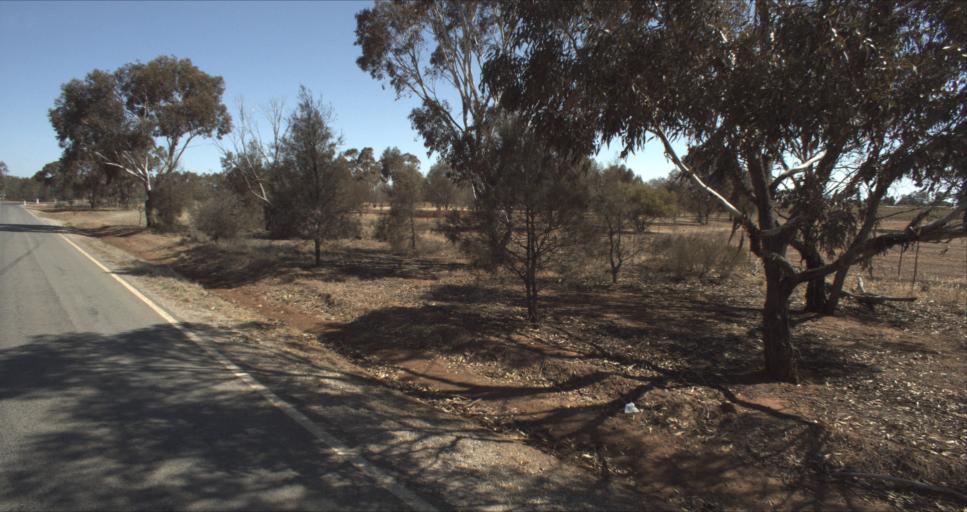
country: AU
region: New South Wales
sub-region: Leeton
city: Leeton
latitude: -34.5033
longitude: 146.4339
